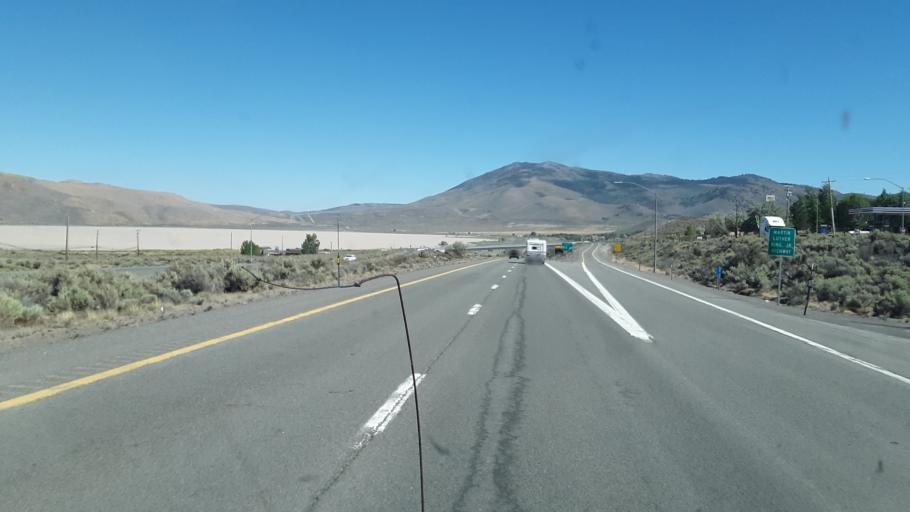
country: US
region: Nevada
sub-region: Washoe County
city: Cold Springs
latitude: 39.6720
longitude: -120.0000
